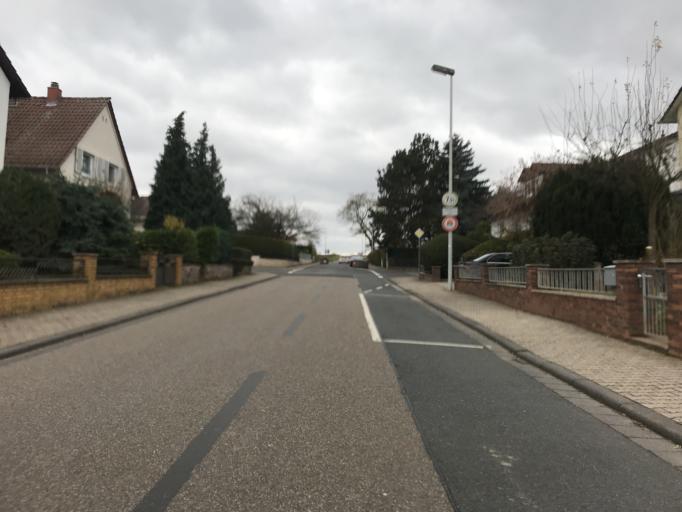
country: DE
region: Rheinland-Pfalz
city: Zornheim
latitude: 49.9128
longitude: 8.2380
